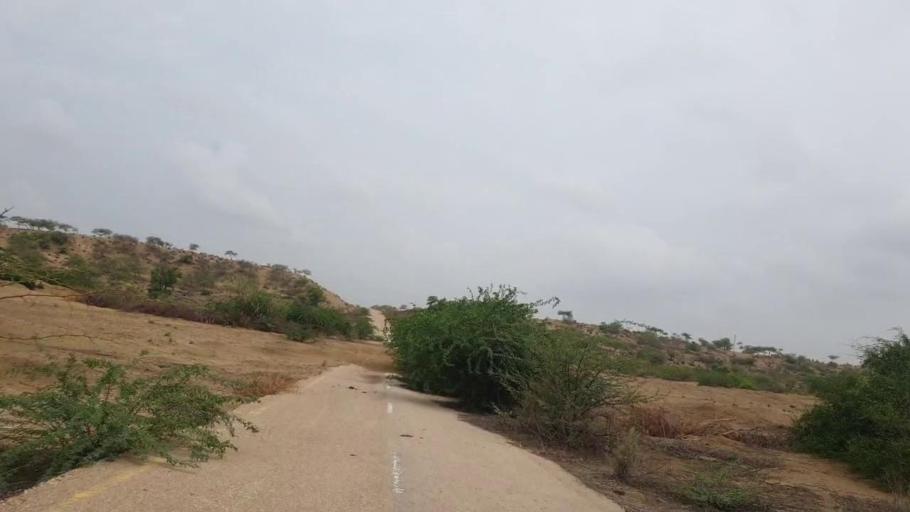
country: PK
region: Sindh
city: Naukot
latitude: 24.6295
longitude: 69.3557
